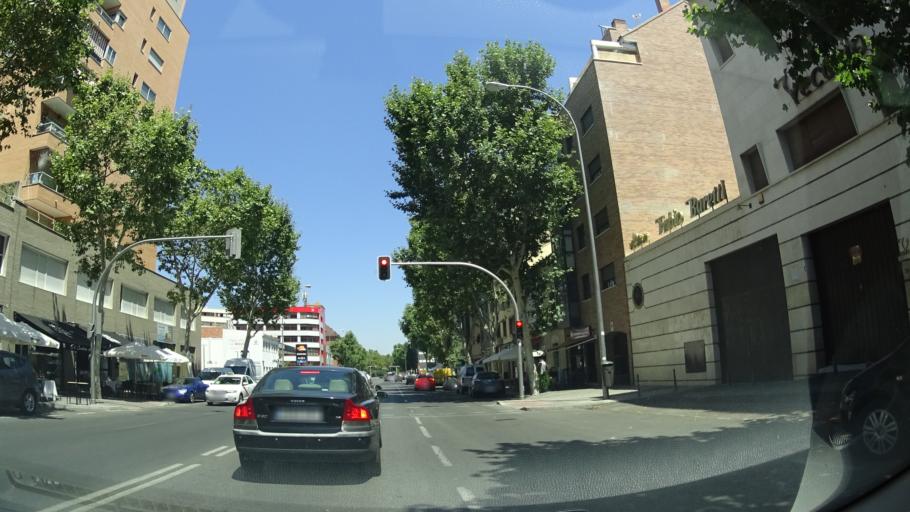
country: ES
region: Madrid
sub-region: Provincia de Madrid
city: Usera
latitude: 40.3822
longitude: -3.6957
